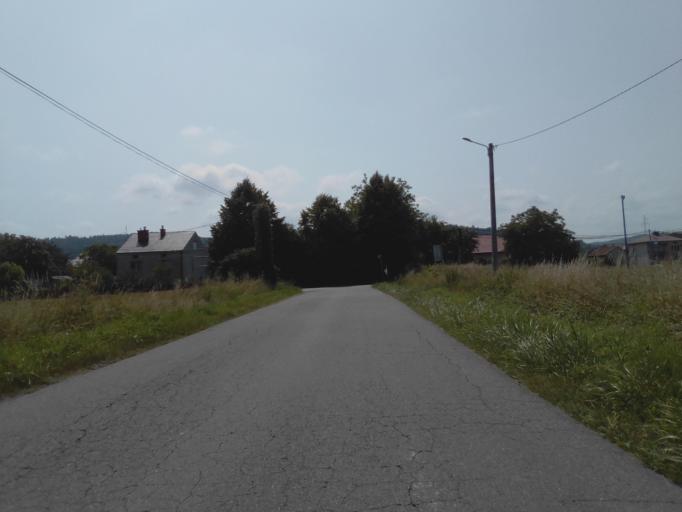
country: PL
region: Subcarpathian Voivodeship
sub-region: Powiat strzyzowski
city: Czudec
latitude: 49.9417
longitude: 21.8164
